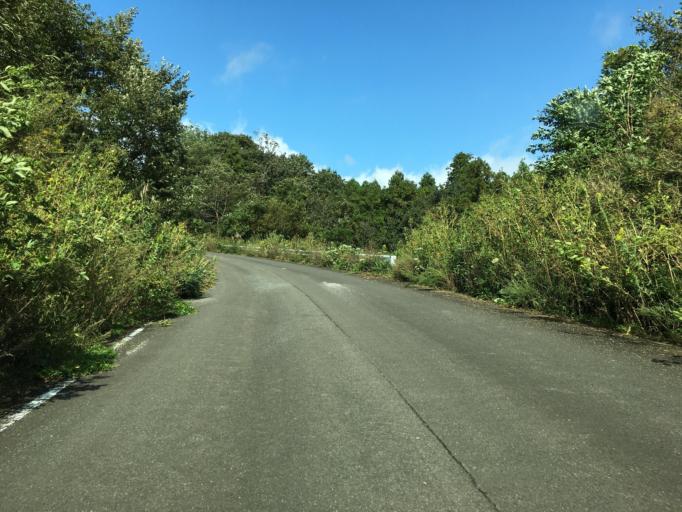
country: JP
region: Fukushima
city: Nihommatsu
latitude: 37.6552
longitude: 140.4189
